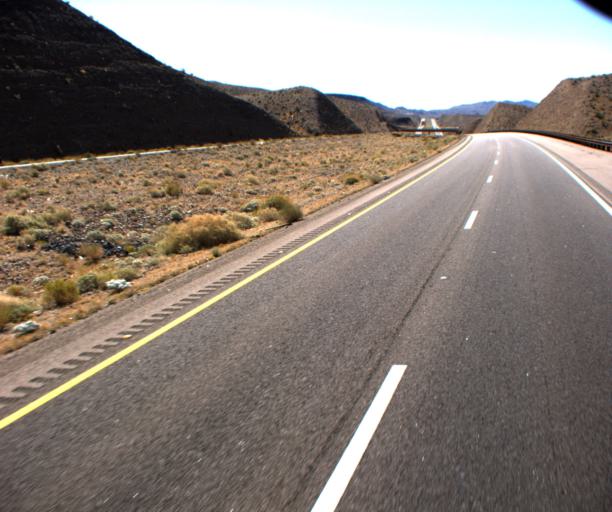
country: US
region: Nevada
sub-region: Clark County
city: Boulder City
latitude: 35.8936
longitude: -114.6250
